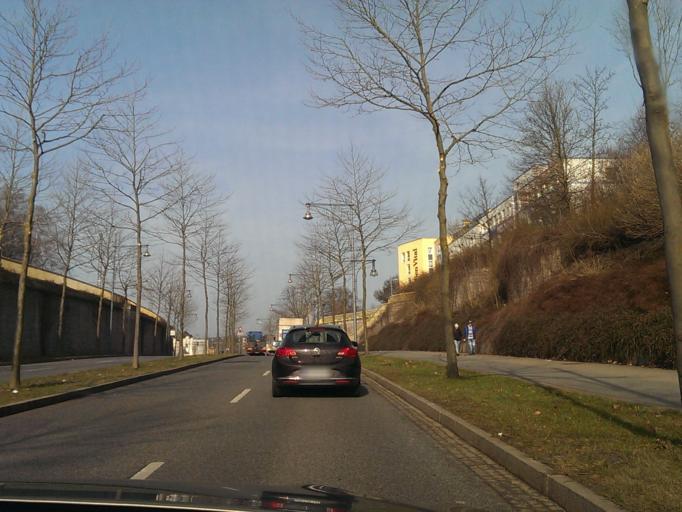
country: DE
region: Saxony
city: Chemnitz
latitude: 50.8263
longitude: 12.9166
